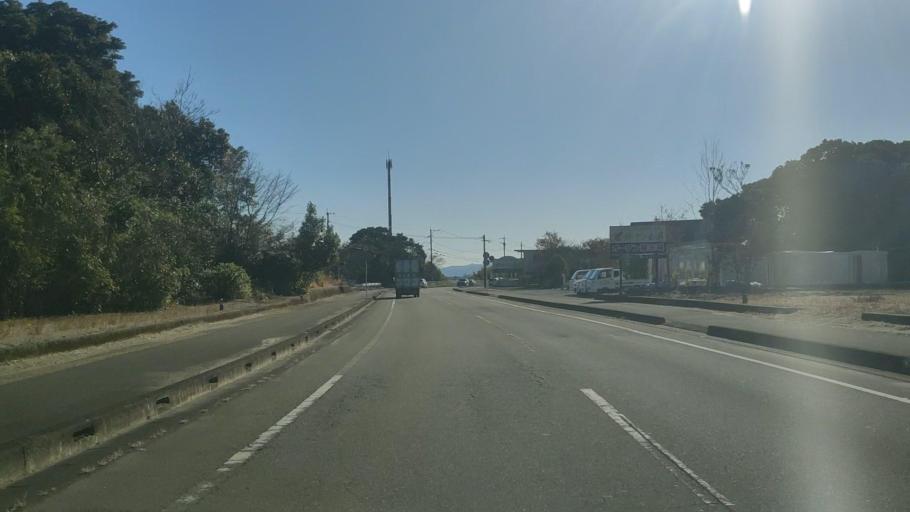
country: JP
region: Miyazaki
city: Miyazaki-shi
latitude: 31.9500
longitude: 131.4601
